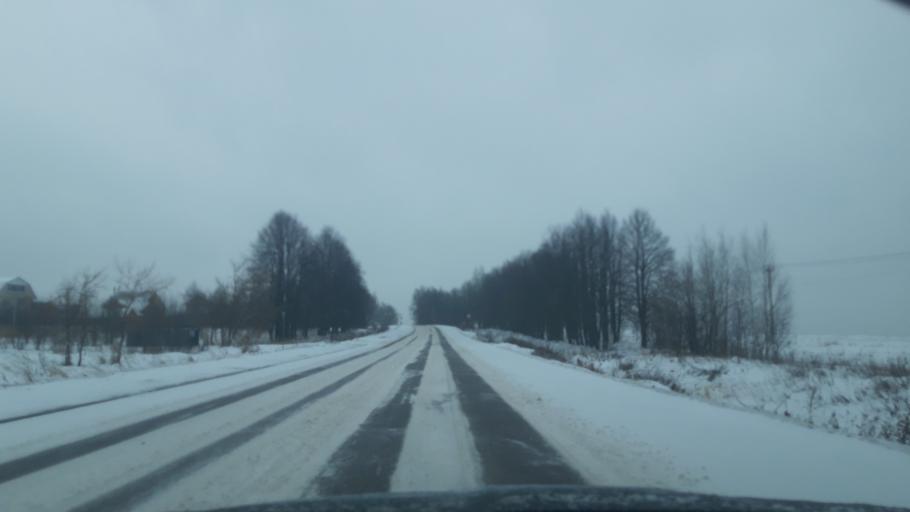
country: RU
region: Moskovskaya
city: Yakhroma
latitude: 56.2994
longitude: 37.4590
